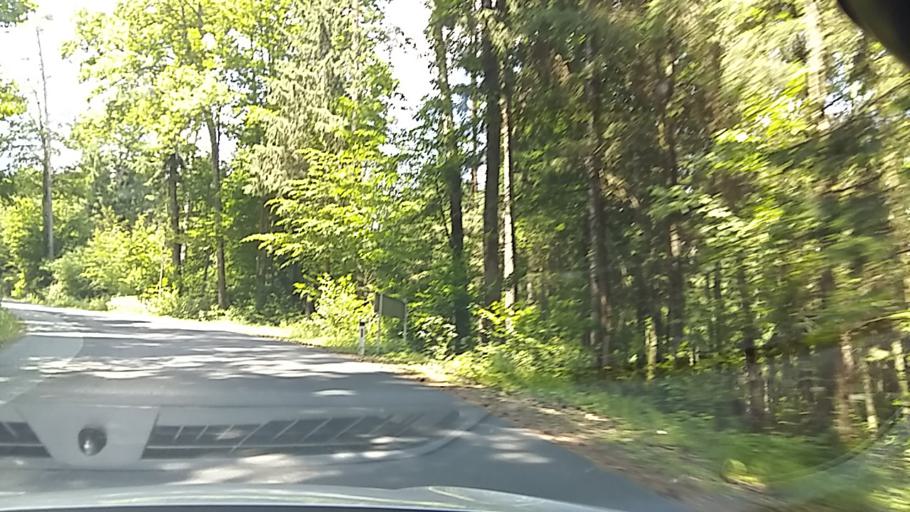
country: AT
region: Styria
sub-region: Politischer Bezirk Hartberg-Fuerstenfeld
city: Bad Blumau
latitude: 47.1209
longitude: 16.0450
